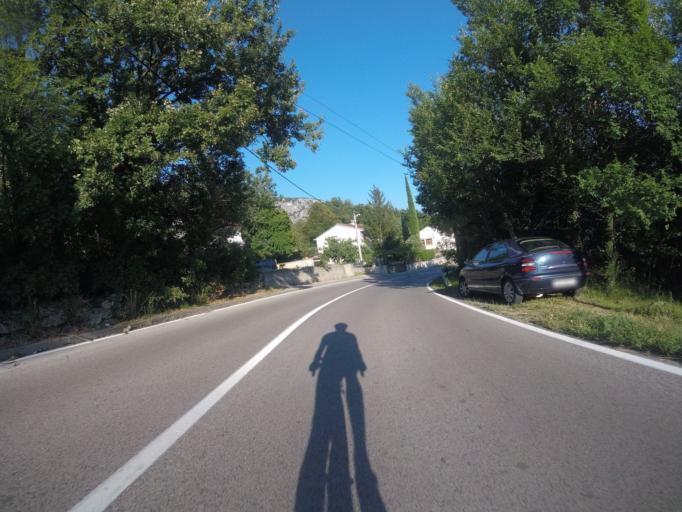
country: HR
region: Primorsko-Goranska
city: Bribir
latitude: 45.1699
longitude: 14.7496
